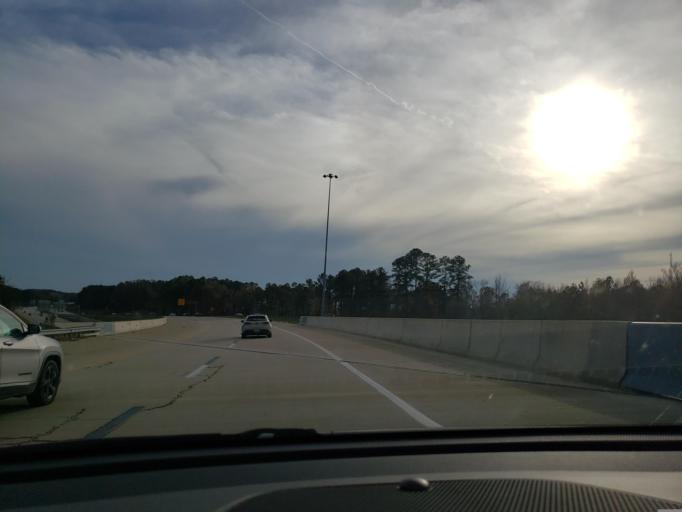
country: US
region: North Carolina
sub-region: Durham County
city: Durham
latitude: 35.9658
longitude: -78.8655
